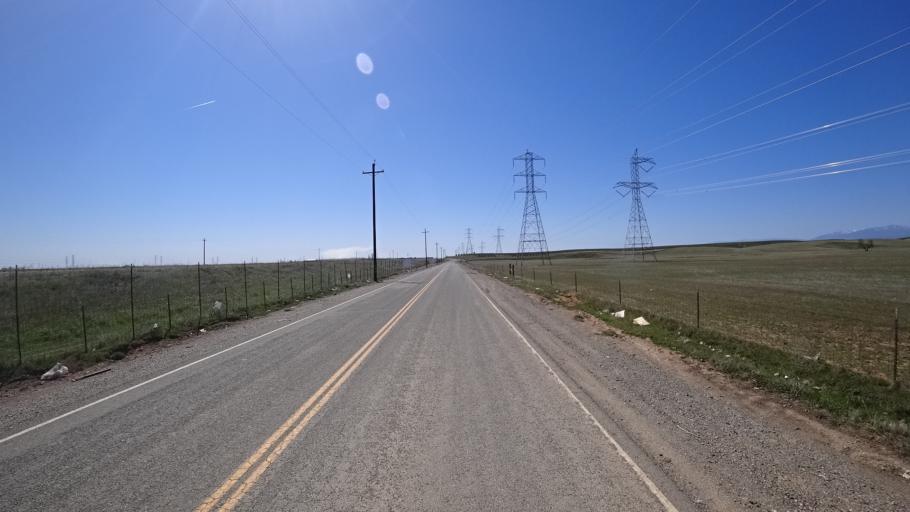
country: US
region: California
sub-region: Glenn County
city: Willows
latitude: 39.6289
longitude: -122.2730
